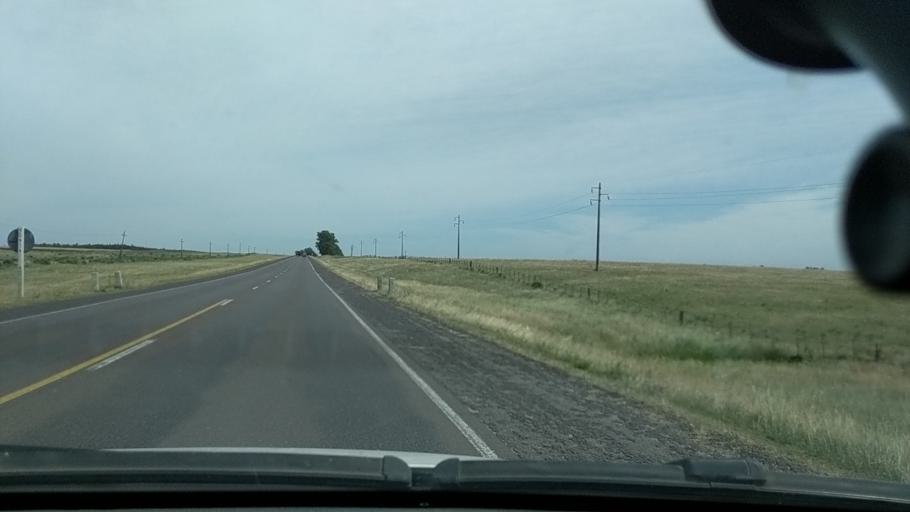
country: UY
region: Durazno
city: Durazno
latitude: -33.4806
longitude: -56.4437
